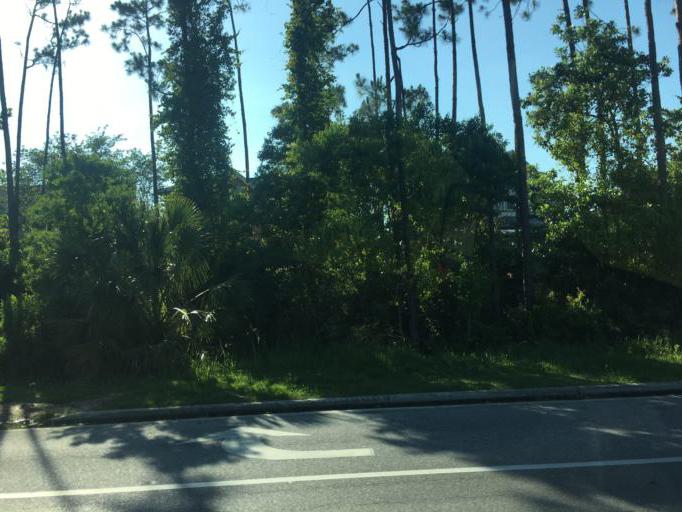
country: US
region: Florida
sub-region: Bay County
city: Panama City Beach
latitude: 30.1975
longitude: -85.8223
